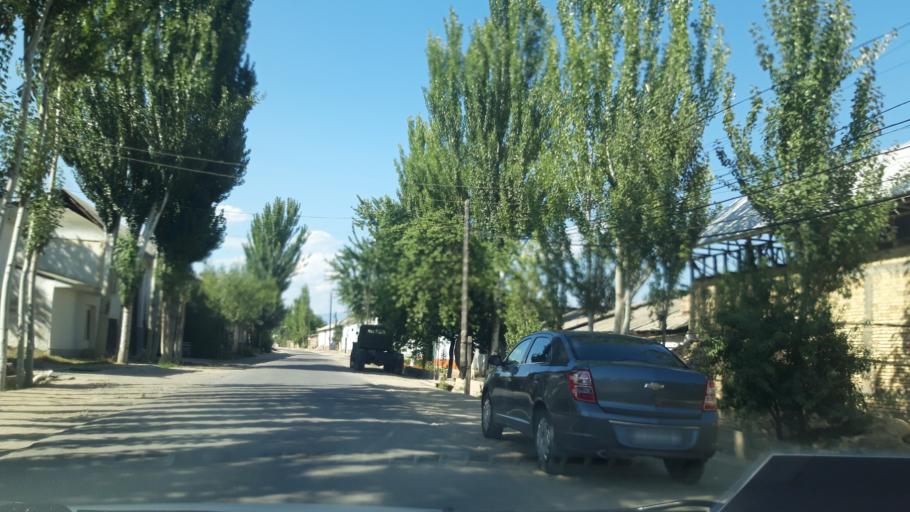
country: UZ
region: Namangan
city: Yangiqo`rg`on
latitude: 41.2031
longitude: 71.7258
